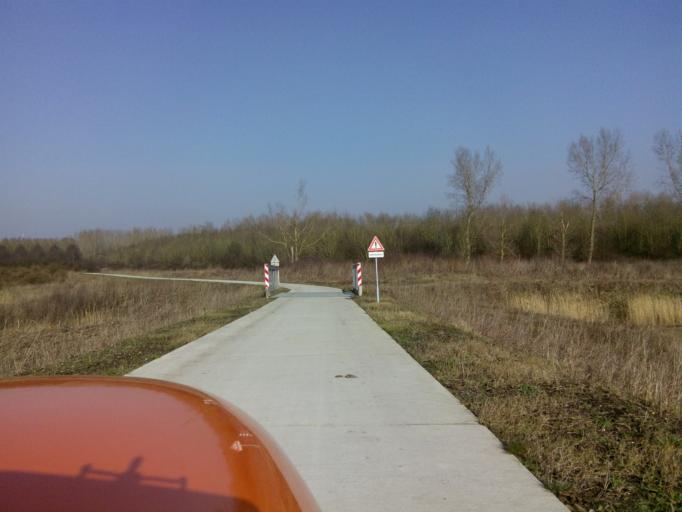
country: NL
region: Flevoland
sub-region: Gemeente Zeewolde
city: Zeewolde
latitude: 52.3268
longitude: 5.4488
